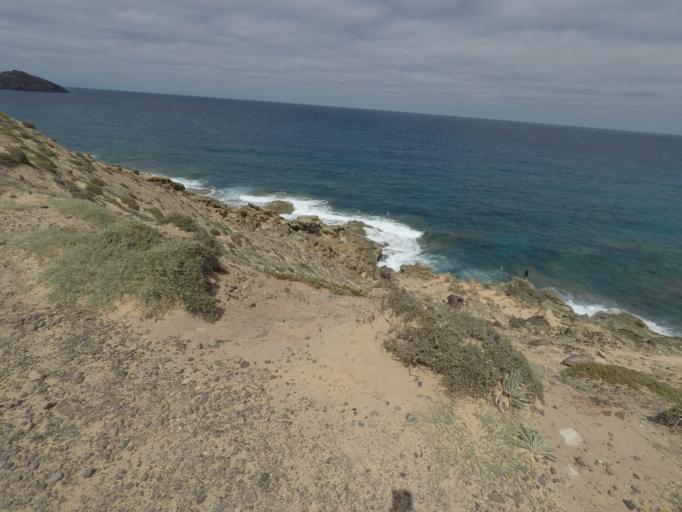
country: PT
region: Madeira
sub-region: Porto Santo
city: Vila de Porto Santo
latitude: 33.0628
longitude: -16.2954
